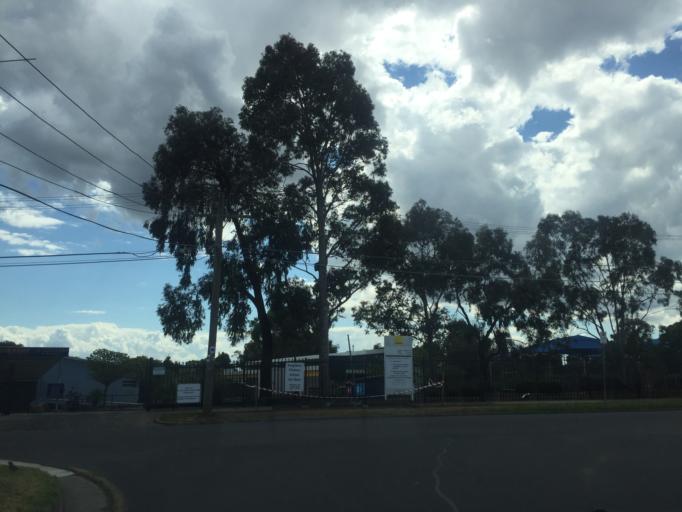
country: AU
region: Victoria
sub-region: Darebin
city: Kingsbury
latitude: -37.7162
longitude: 145.0377
